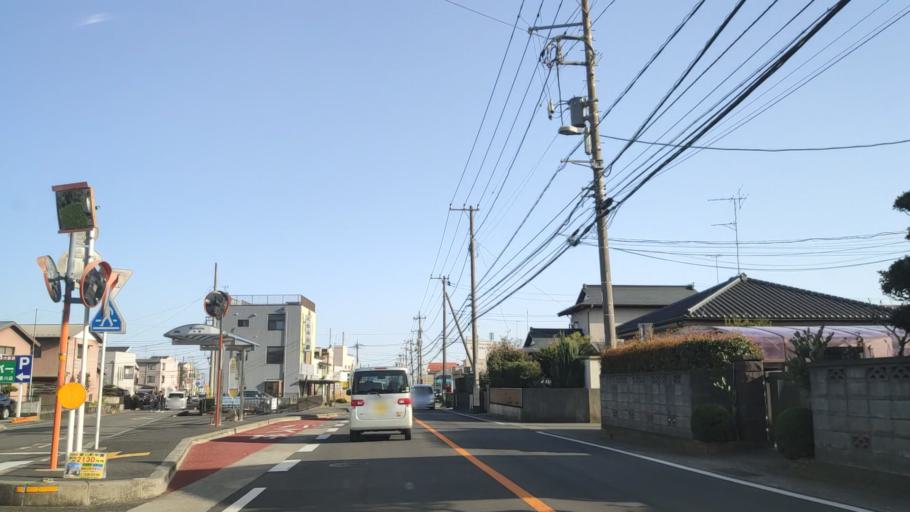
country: JP
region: Kanagawa
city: Zama
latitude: 35.5193
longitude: 139.3313
